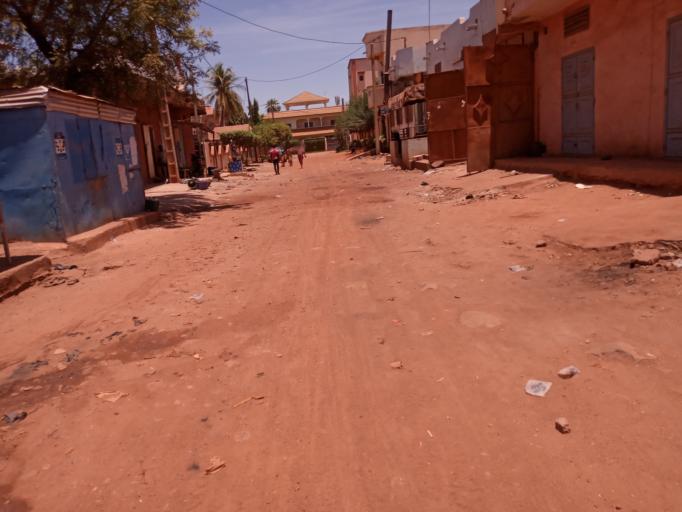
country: ML
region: Bamako
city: Bamako
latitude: 12.5847
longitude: -7.9555
